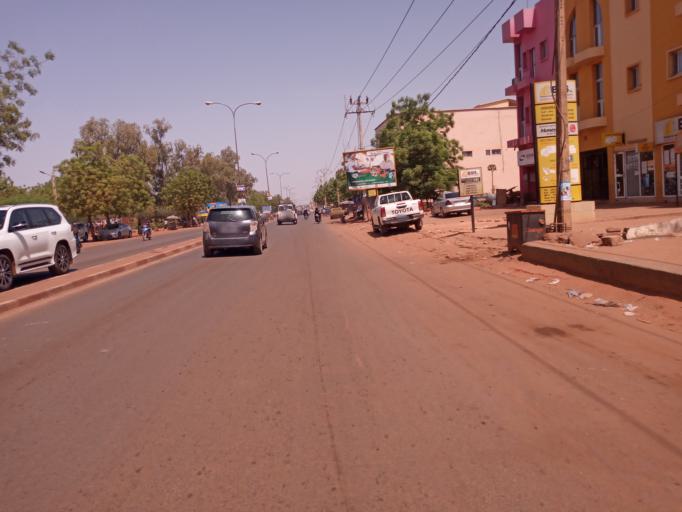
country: ML
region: Bamako
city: Bamako
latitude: 12.6643
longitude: -7.9409
